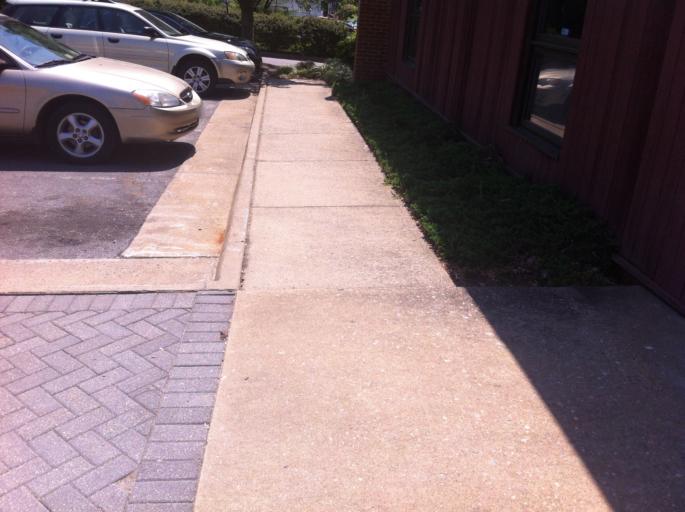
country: US
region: Virginia
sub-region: Henrico County
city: Dumbarton
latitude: 37.5777
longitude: -77.5111
